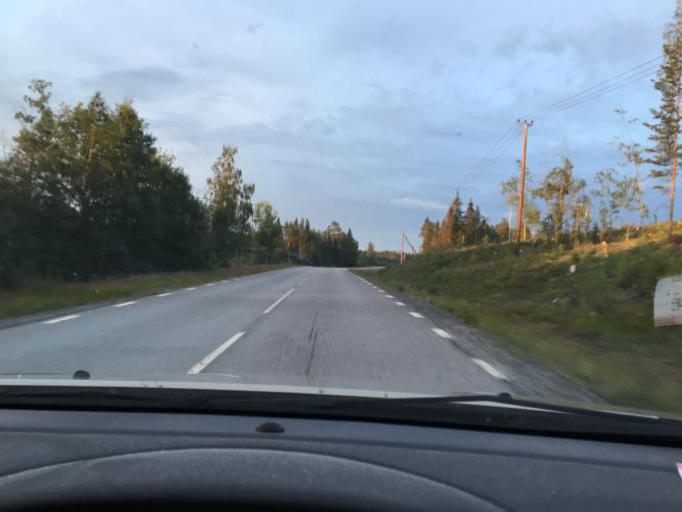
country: SE
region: Norrbotten
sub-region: Lulea Kommun
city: Ranea
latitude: 66.0402
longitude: 22.3127
